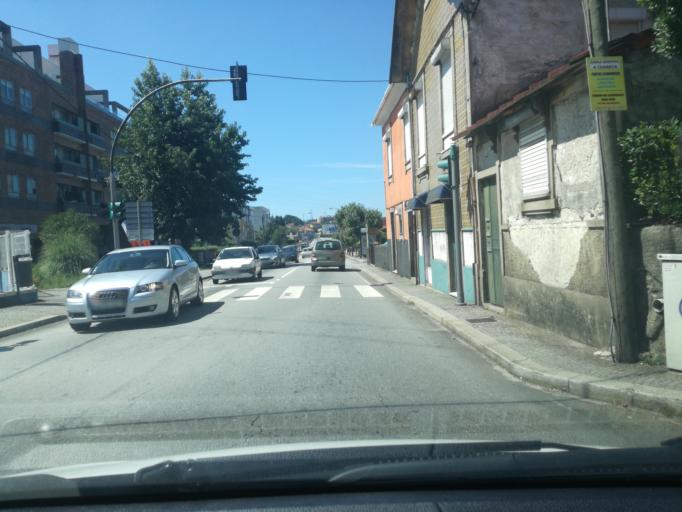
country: PT
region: Porto
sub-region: Maia
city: Nogueira
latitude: 41.2344
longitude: -8.5952
